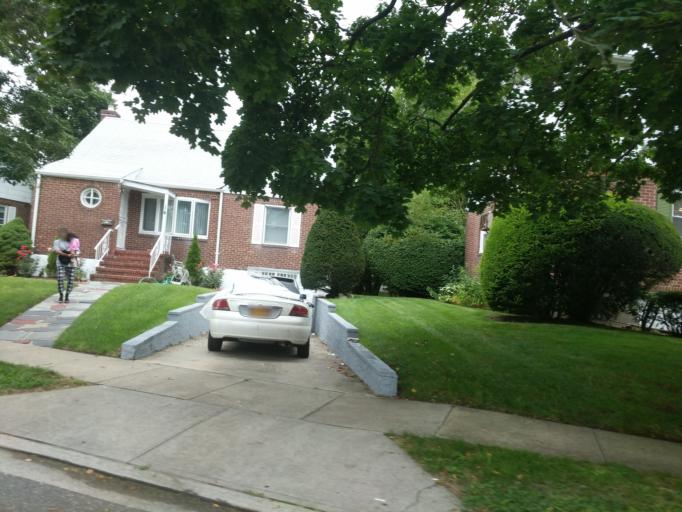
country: US
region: New York
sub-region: Nassau County
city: South Valley Stream
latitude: 40.6582
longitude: -73.7118
